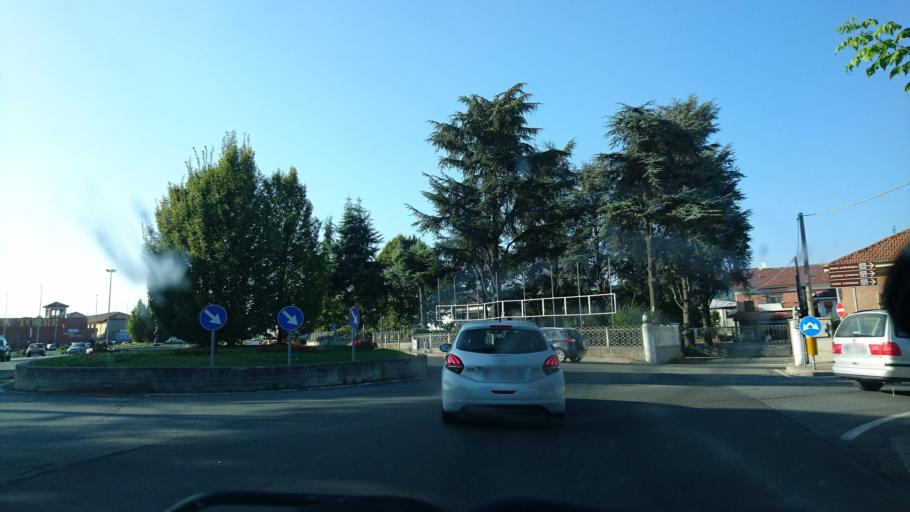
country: IT
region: Piedmont
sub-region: Provincia di Alessandria
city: Acqui Terme
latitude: 44.6680
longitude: 8.4567
